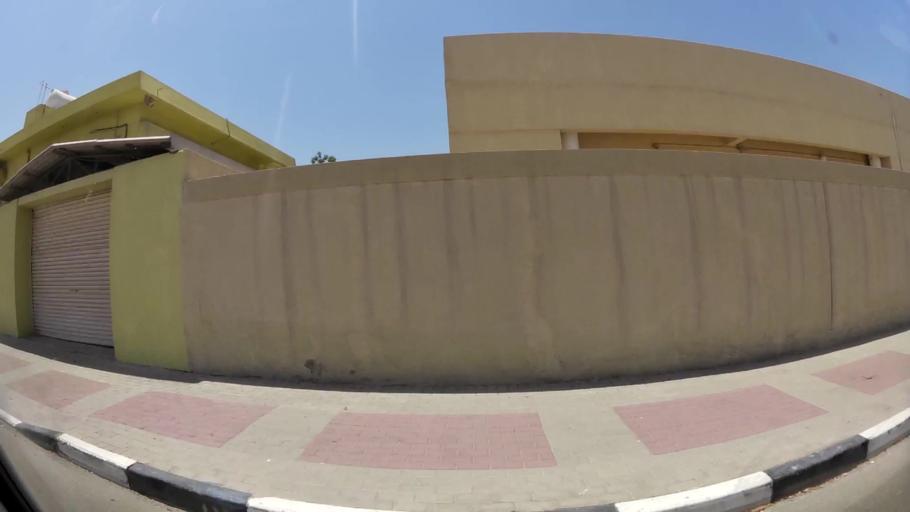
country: AE
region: Ash Shariqah
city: Sharjah
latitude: 25.2960
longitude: 55.3353
